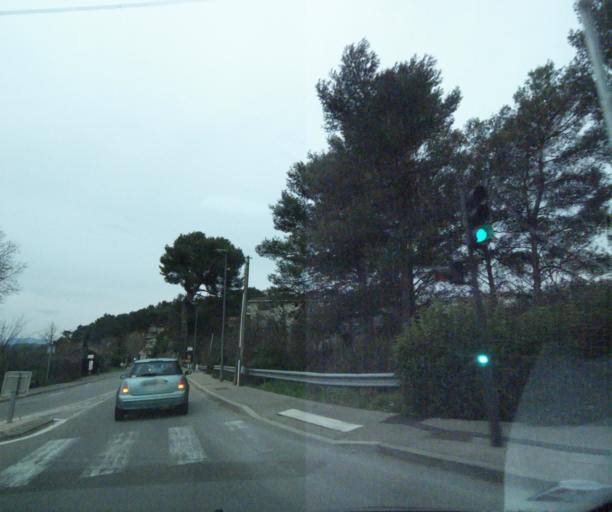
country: FR
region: Provence-Alpes-Cote d'Azur
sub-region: Departement des Bouches-du-Rhone
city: Aix-en-Provence
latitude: 43.5408
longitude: 5.4573
